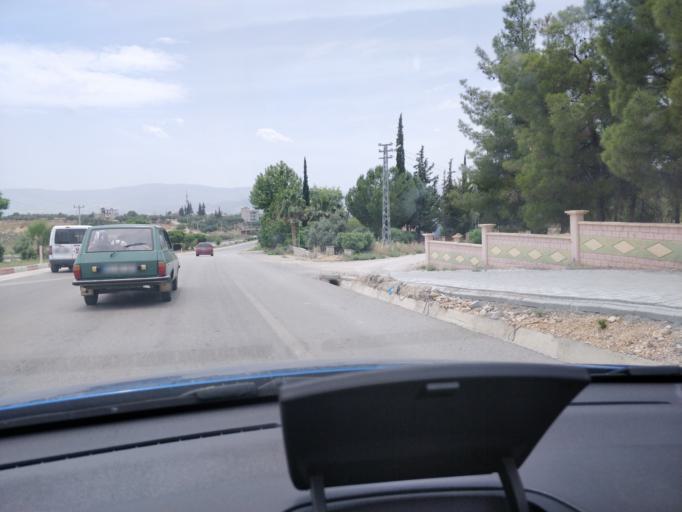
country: TR
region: Mersin
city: Mut
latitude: 36.6156
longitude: 33.4412
